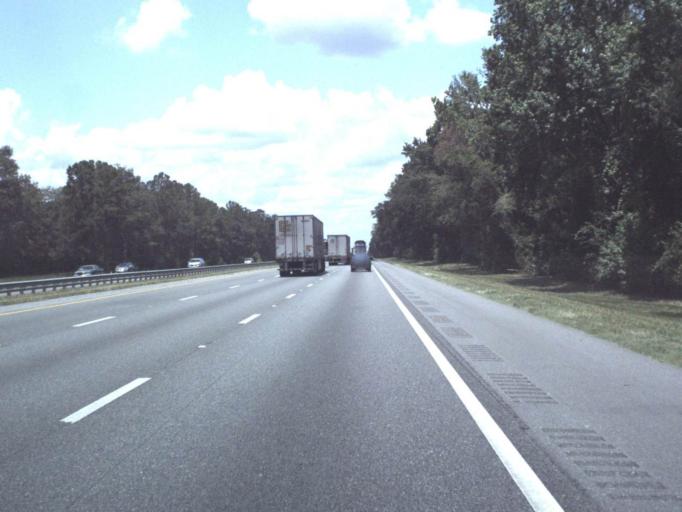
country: US
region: Florida
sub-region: Hamilton County
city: Jasper
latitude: 30.4668
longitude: -82.9625
